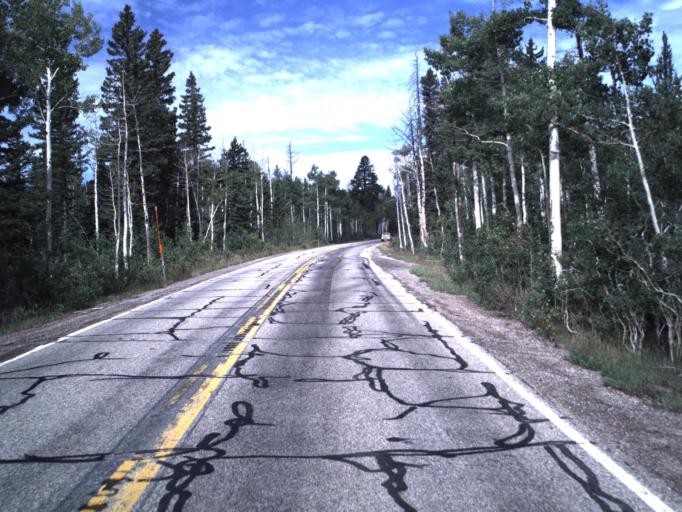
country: US
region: Utah
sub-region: Iron County
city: Parowan
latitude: 37.5180
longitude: -112.7190
